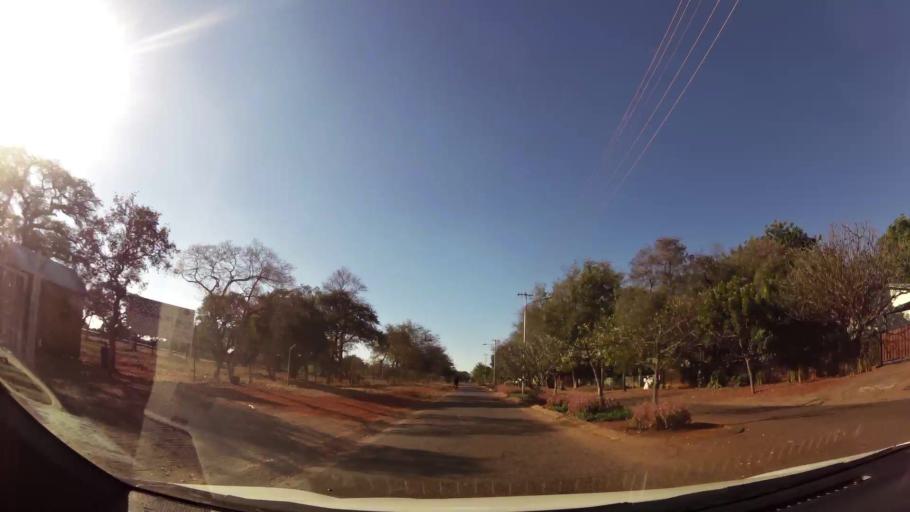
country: ZA
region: Limpopo
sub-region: Waterberg District Municipality
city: Mokopane
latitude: -24.1990
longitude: 29.0094
